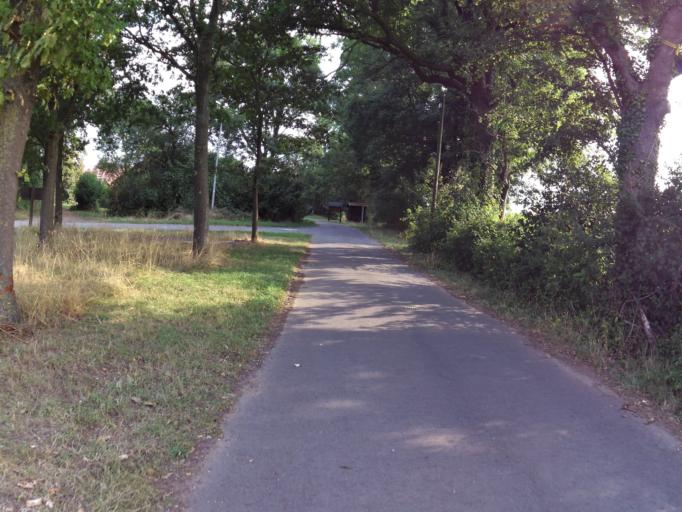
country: DE
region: Lower Saxony
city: Raddestorf
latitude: 52.4512
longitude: 9.0099
